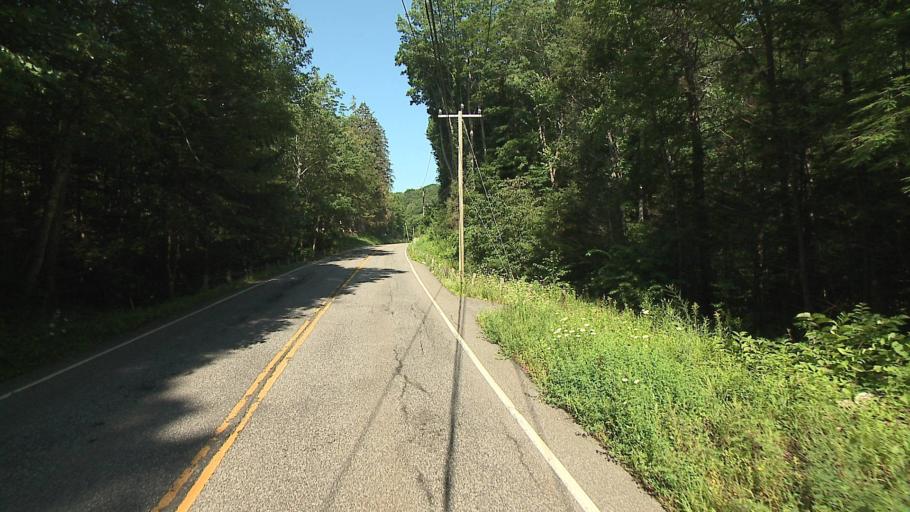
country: US
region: Connecticut
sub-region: Litchfield County
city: Kent
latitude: 41.8223
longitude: -73.3941
